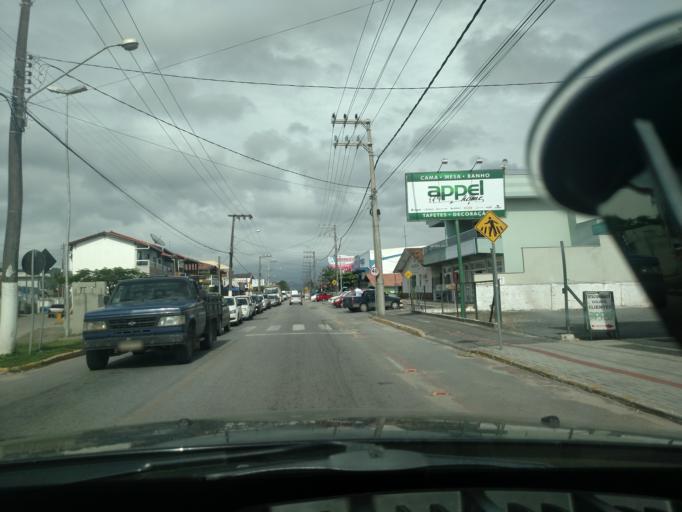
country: BR
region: Santa Catarina
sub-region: Porto Belo
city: Porto Belo
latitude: -27.1582
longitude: -48.5631
